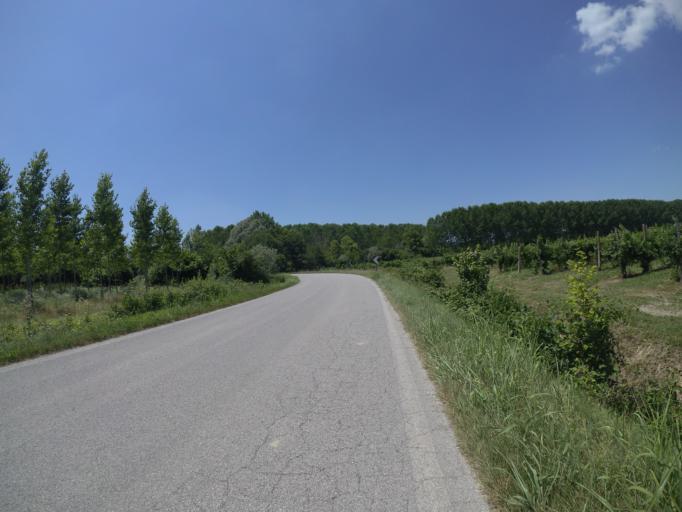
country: IT
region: Friuli Venezia Giulia
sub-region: Provincia di Udine
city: Rivignano
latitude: 45.9045
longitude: 13.0452
